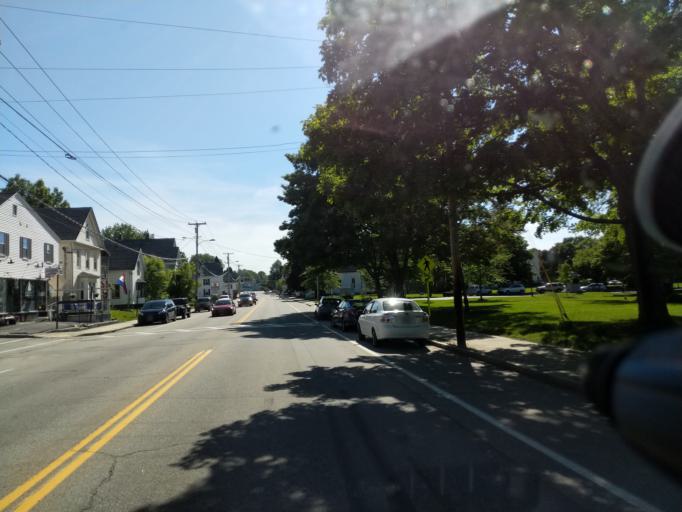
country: US
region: Maine
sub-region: Cumberland County
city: Westbrook
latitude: 43.6786
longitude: -70.3571
